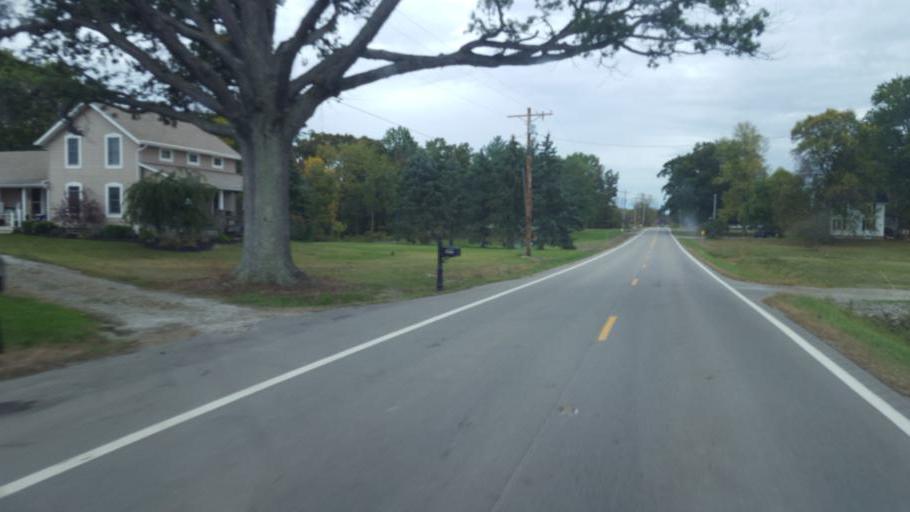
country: US
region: Ohio
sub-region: Huron County
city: Wakeman
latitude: 41.2214
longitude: -82.3954
